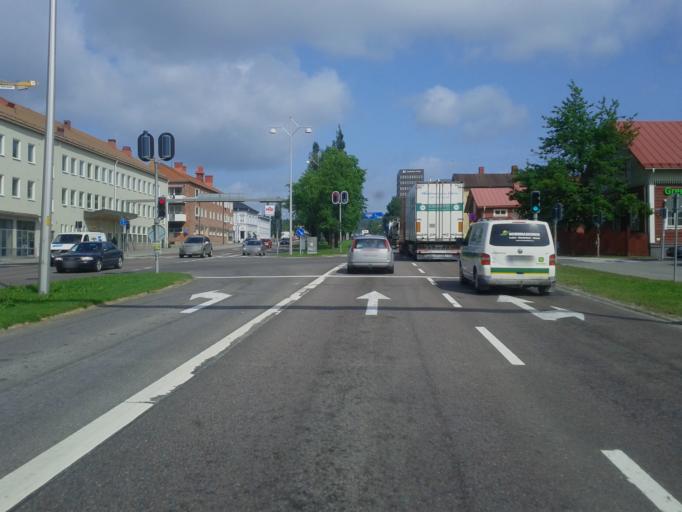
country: SE
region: Vaesterbotten
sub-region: Skelleftea Kommun
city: Skelleftea
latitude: 64.7489
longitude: 20.9604
